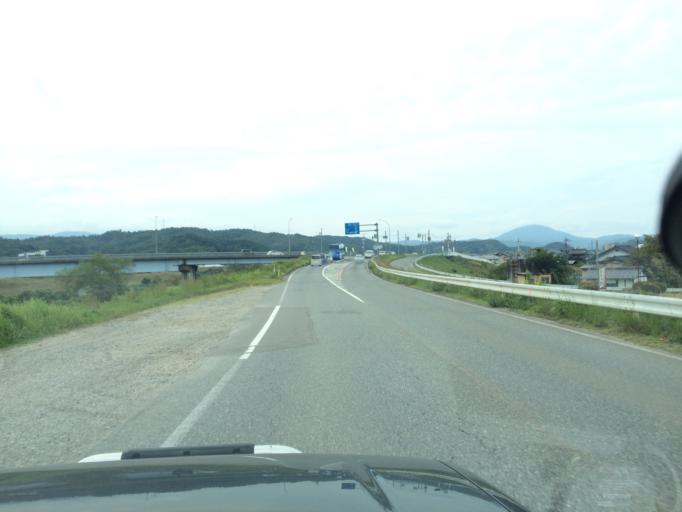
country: JP
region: Hyogo
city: Toyooka
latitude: 35.5123
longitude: 134.8276
